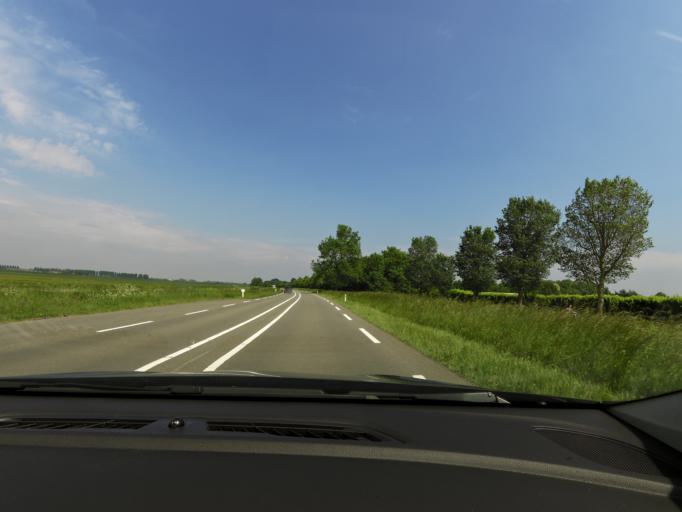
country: NL
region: Zeeland
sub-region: Gemeente Tholen
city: Tholen
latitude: 51.5389
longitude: 4.1958
